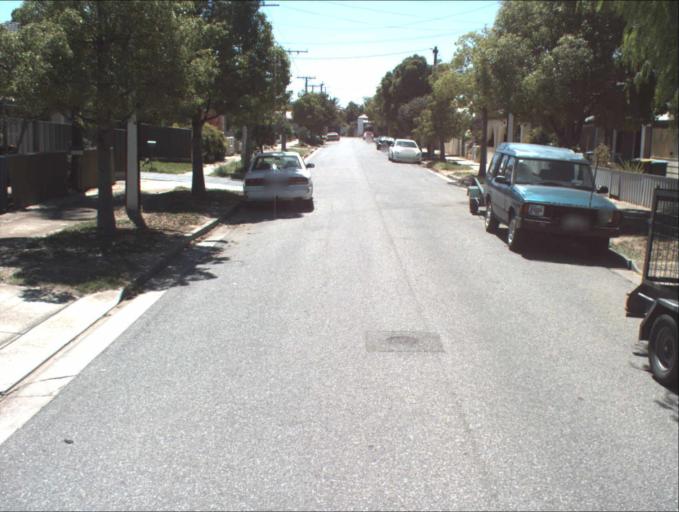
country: AU
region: South Australia
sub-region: Port Adelaide Enfield
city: Birkenhead
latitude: -34.8460
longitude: 138.4923
